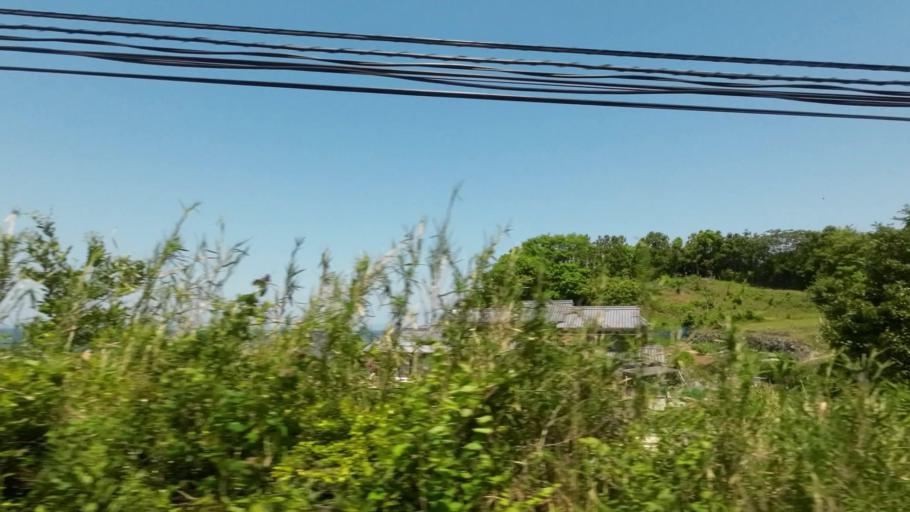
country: JP
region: Ehime
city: Hojo
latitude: 34.0238
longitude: 132.8190
